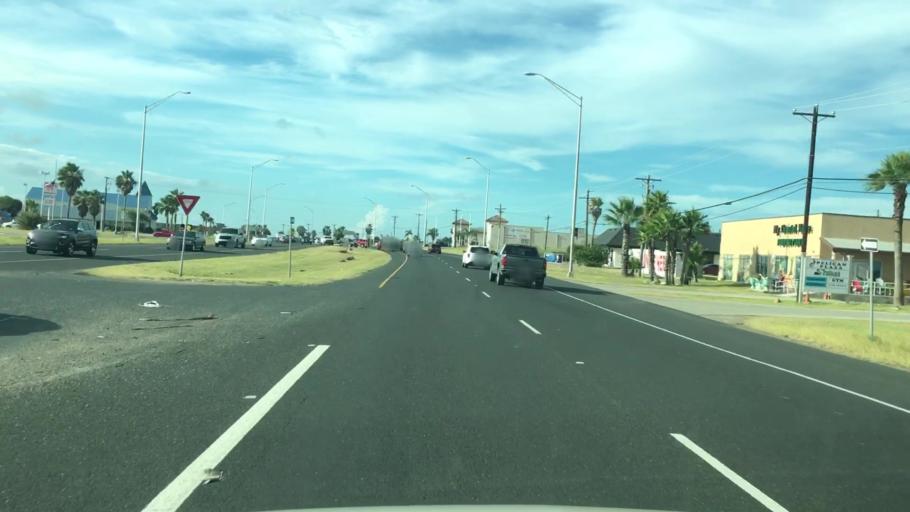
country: US
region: Texas
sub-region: Nueces County
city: Corpus Christi
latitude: 27.6221
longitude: -97.2216
